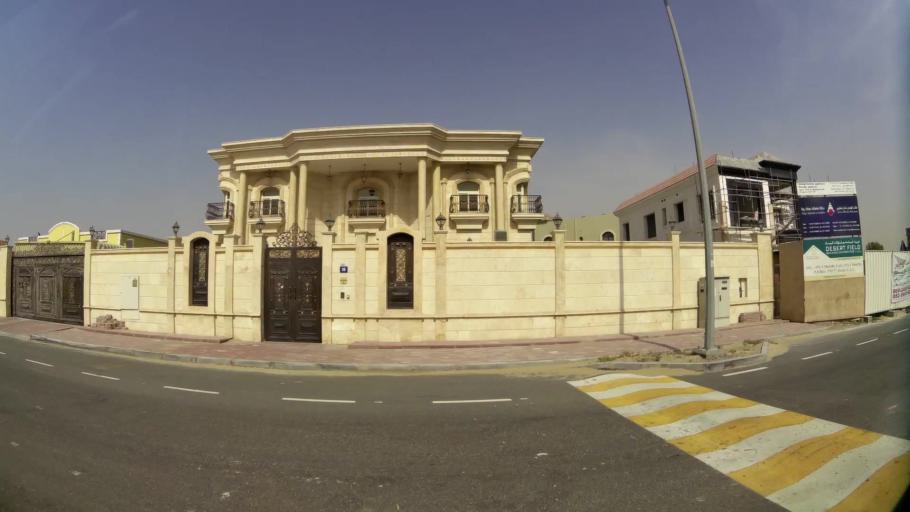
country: AE
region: Ash Shariqah
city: Sharjah
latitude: 25.2653
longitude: 55.4608
